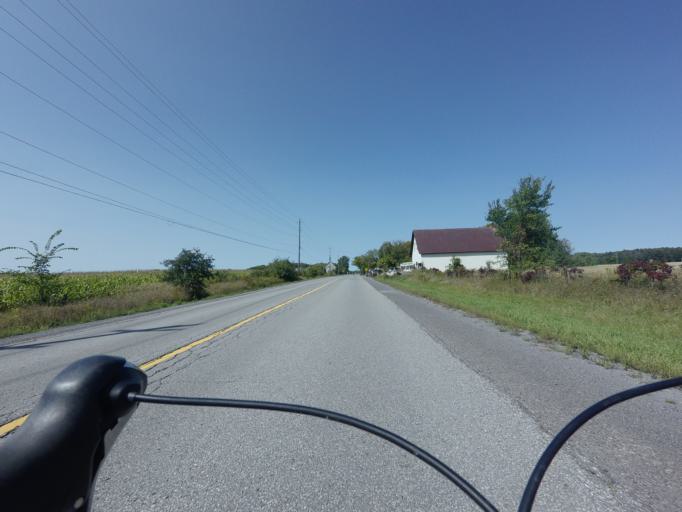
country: CA
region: Ontario
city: Arnprior
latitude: 45.4734
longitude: -76.1134
